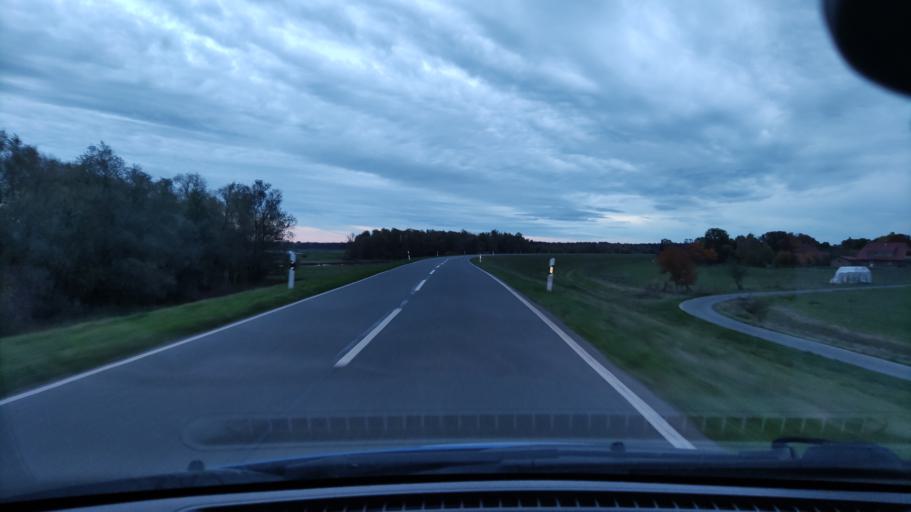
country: DE
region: Lower Saxony
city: Gorleben
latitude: 53.0543
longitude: 11.3895
